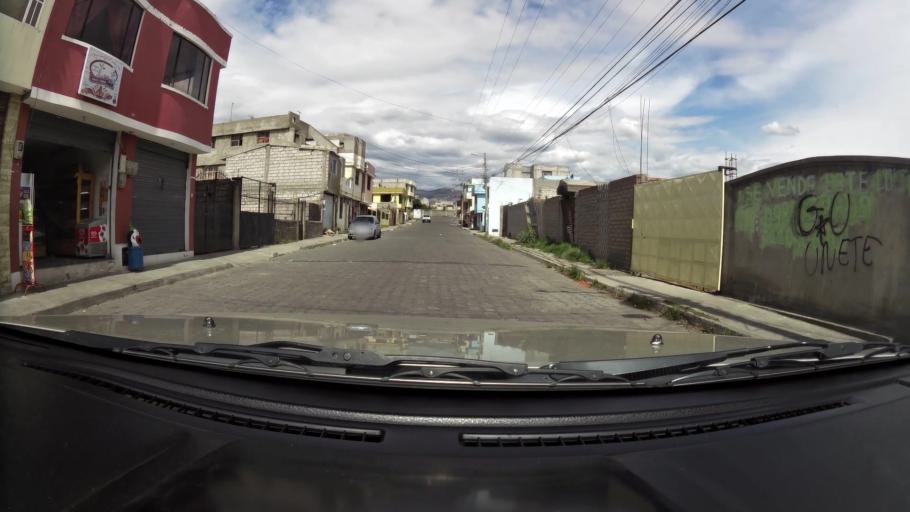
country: EC
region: Cotopaxi
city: Latacunga
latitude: -0.9267
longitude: -78.6083
